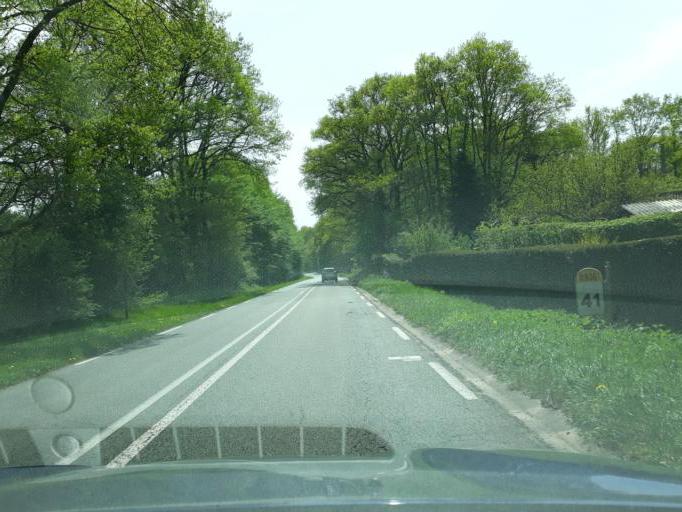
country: FR
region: Ile-de-France
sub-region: Departement des Yvelines
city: Saint-Leger-en-Yvelines
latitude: 48.6930
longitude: 1.7706
